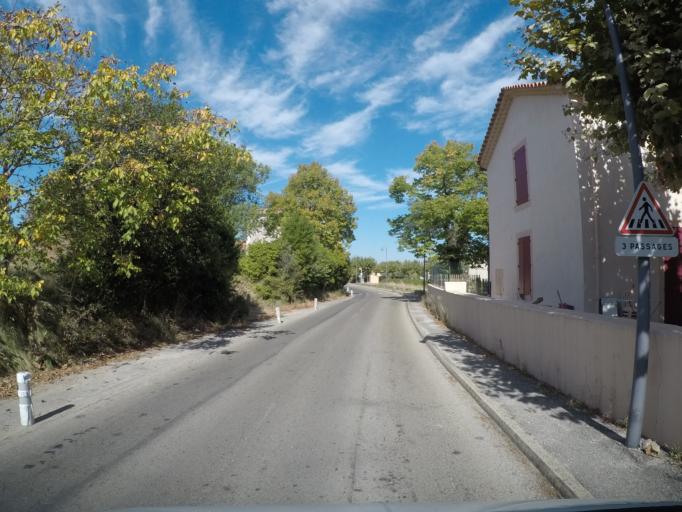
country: FR
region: Languedoc-Roussillon
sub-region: Departement du Gard
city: Boisset-et-Gaujac
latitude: 44.0217
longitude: 3.9962
